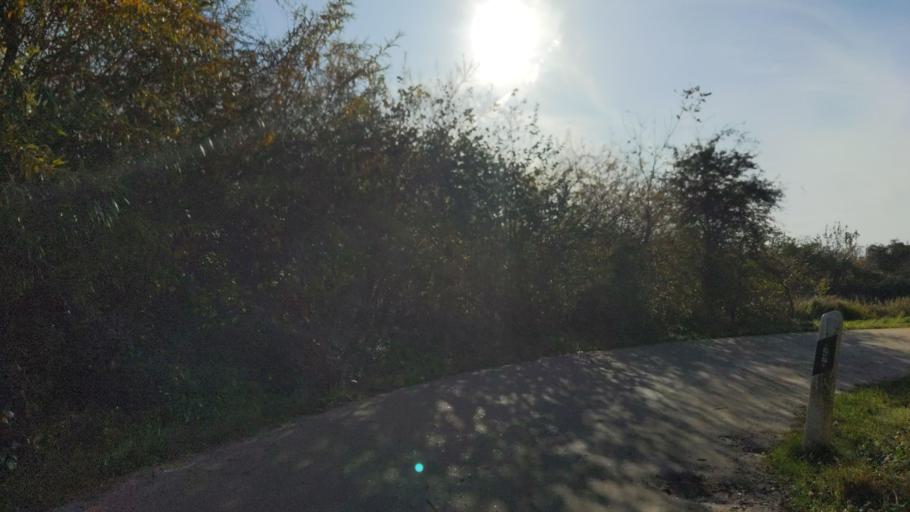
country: DE
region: Schleswig-Holstein
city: Eutin
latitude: 54.1191
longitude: 10.6178
